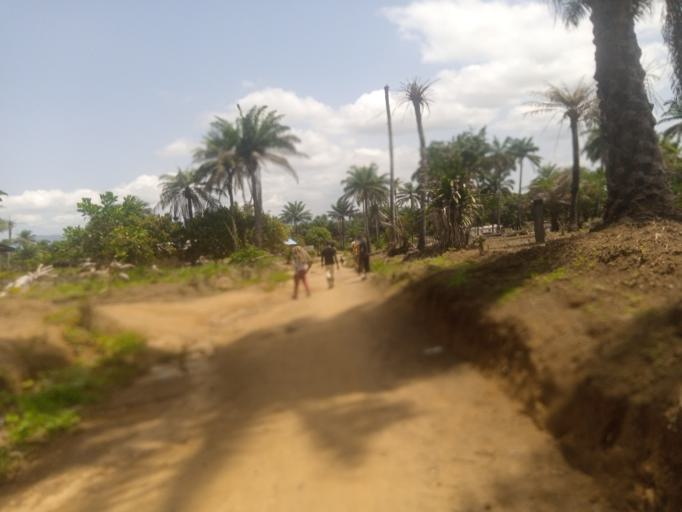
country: SL
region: Western Area
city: Waterloo
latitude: 8.3187
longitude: -13.0072
